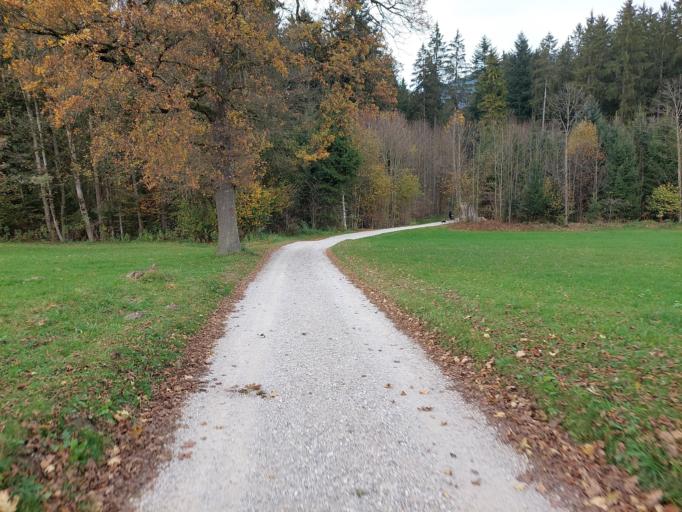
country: AT
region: Tyrol
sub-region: Politischer Bezirk Kufstein
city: Angath
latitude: 47.5031
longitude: 12.0421
